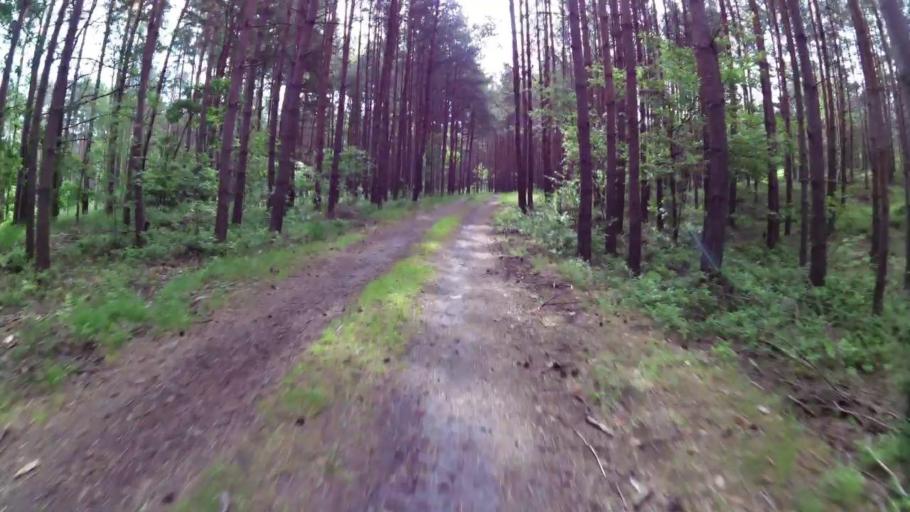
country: PL
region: West Pomeranian Voivodeship
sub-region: Swinoujscie
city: Swinoujscie
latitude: 53.9073
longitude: 14.3209
